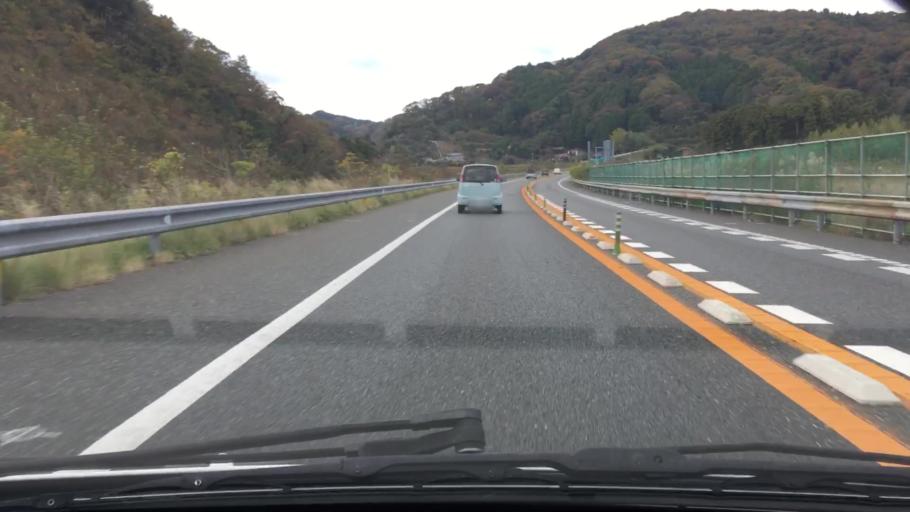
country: JP
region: Chiba
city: Futtsu
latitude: 35.2086
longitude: 139.8822
